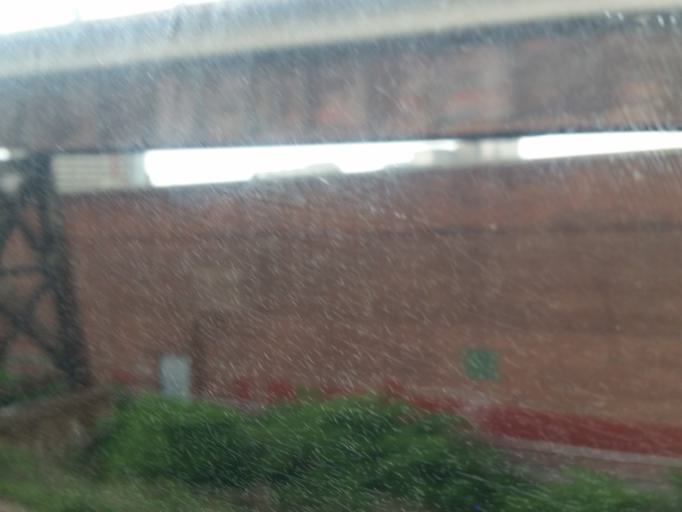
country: US
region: New Jersey
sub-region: Hudson County
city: Harrison
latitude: 40.7380
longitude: -74.1585
